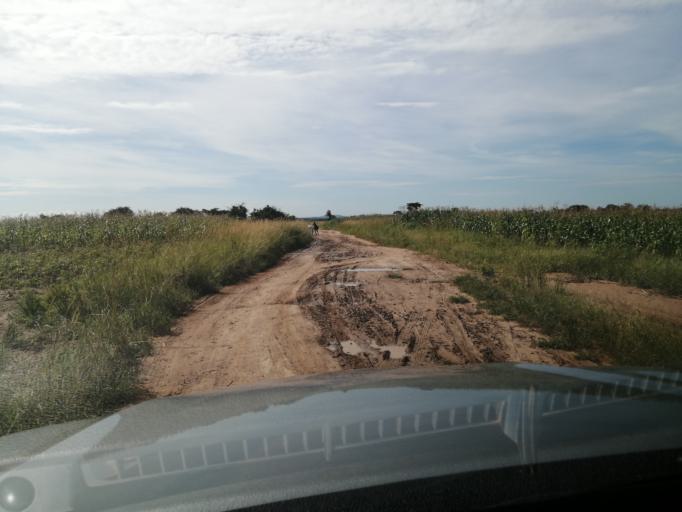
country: ZM
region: Central
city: Chibombo
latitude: -14.9300
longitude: 27.7850
